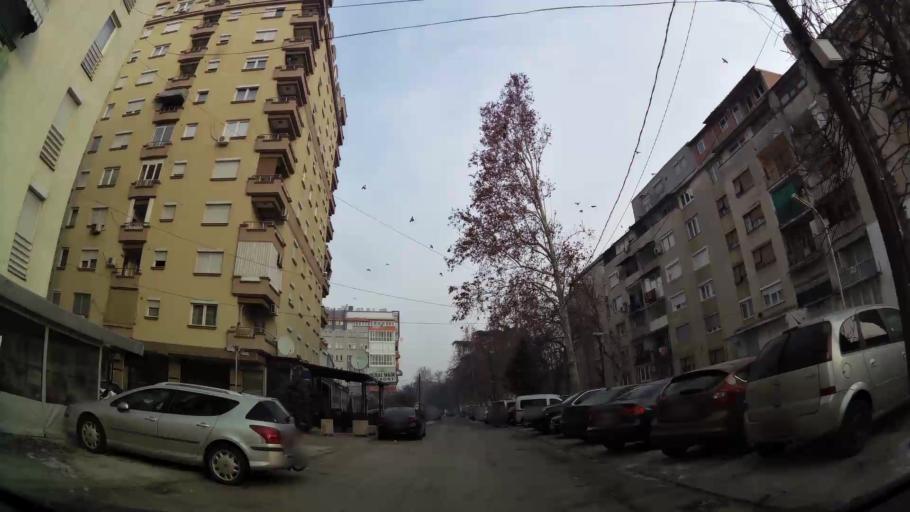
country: MK
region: Cair
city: Cair
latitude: 42.0173
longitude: 21.4454
